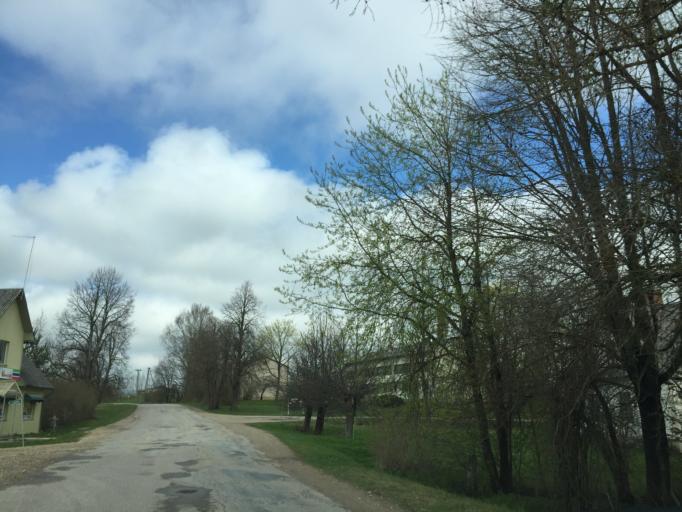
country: EE
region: Valgamaa
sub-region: Valga linn
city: Valga
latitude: 57.5468
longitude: 26.2953
